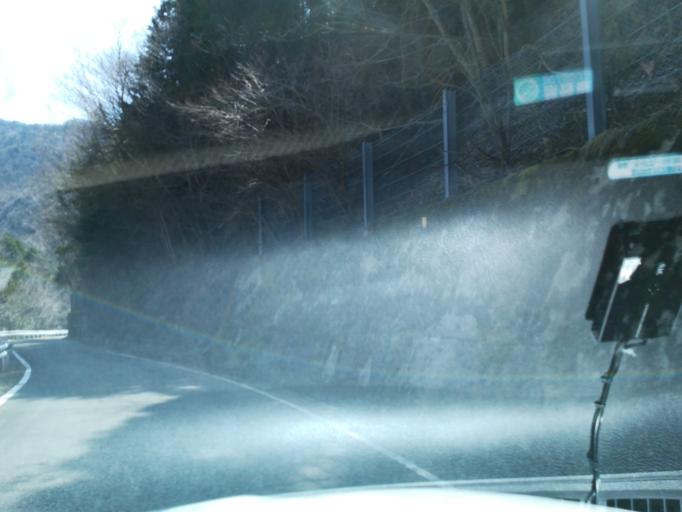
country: JP
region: Tokushima
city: Wakimachi
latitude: 33.8658
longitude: 134.0690
